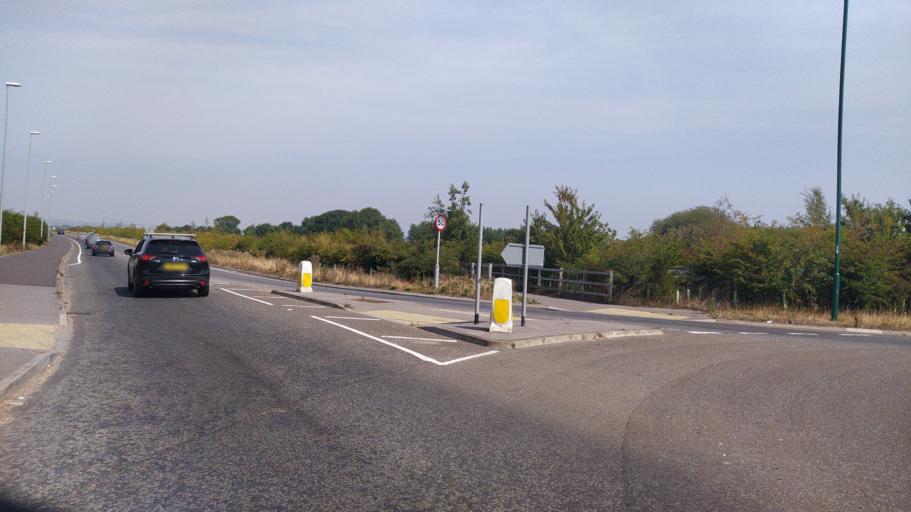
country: GB
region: England
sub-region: West Sussex
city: Barnham
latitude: 50.8029
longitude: -0.6454
